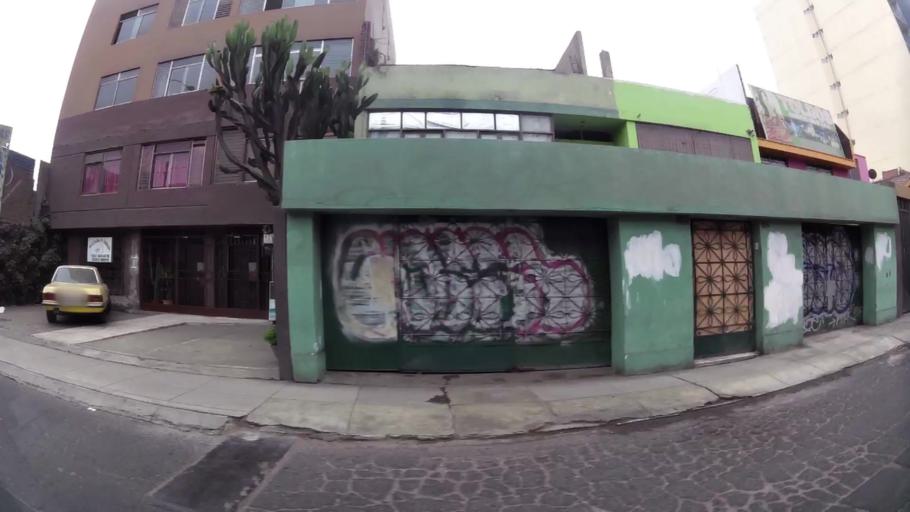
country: PE
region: Lima
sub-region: Lima
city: Surco
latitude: -12.1309
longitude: -76.9999
